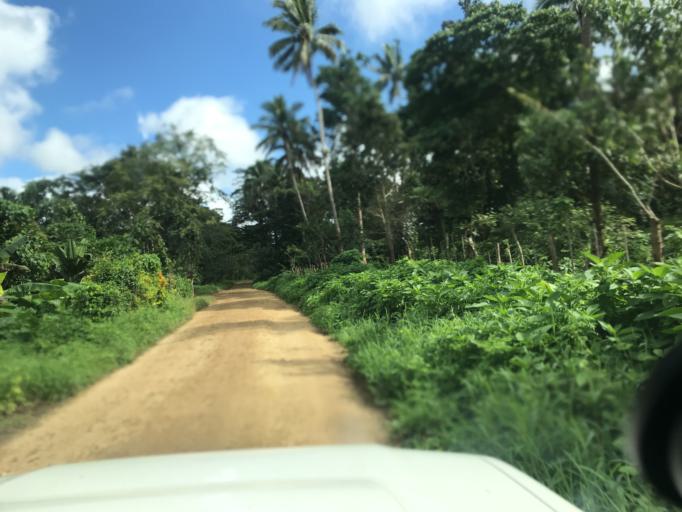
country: VU
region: Sanma
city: Luganville
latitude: -15.4746
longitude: 167.0849
